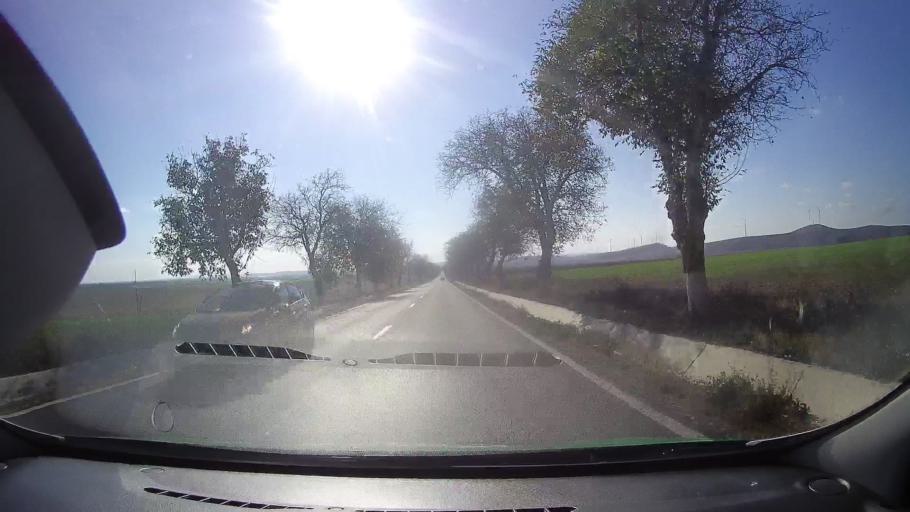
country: RO
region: Tulcea
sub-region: Comuna Ceamurlia de Jos
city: Ceamurlia de Jos
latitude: 44.8027
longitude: 28.6907
